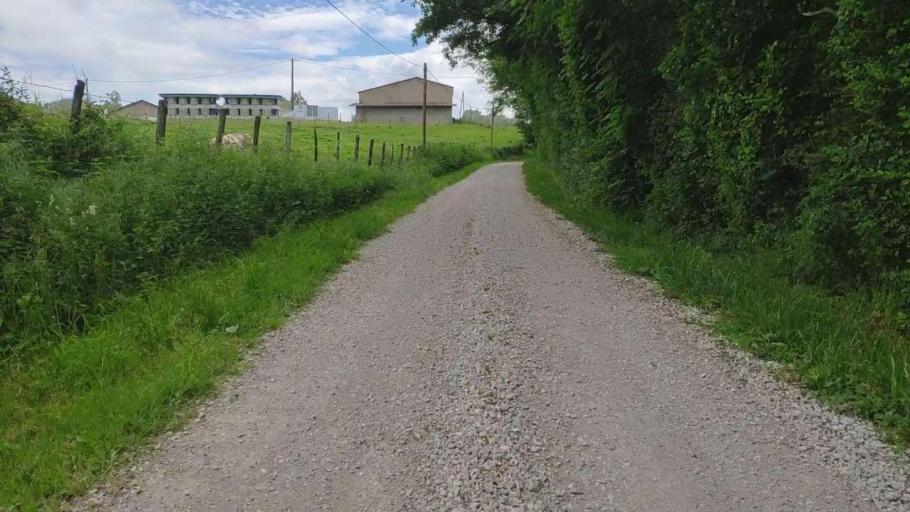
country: FR
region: Franche-Comte
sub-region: Departement du Jura
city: Montmorot
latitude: 46.7503
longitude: 5.5508
